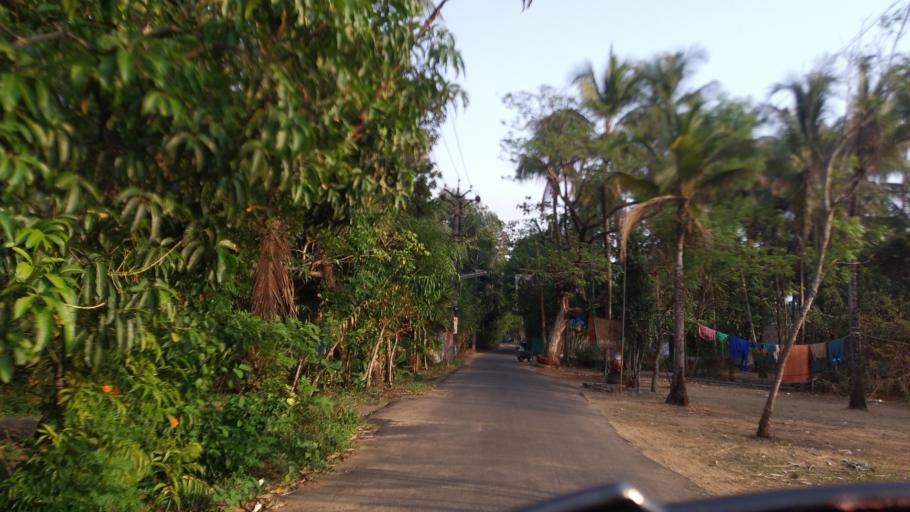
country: IN
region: Kerala
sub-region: Thrissur District
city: Thanniyam
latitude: 10.4270
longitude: 76.0811
